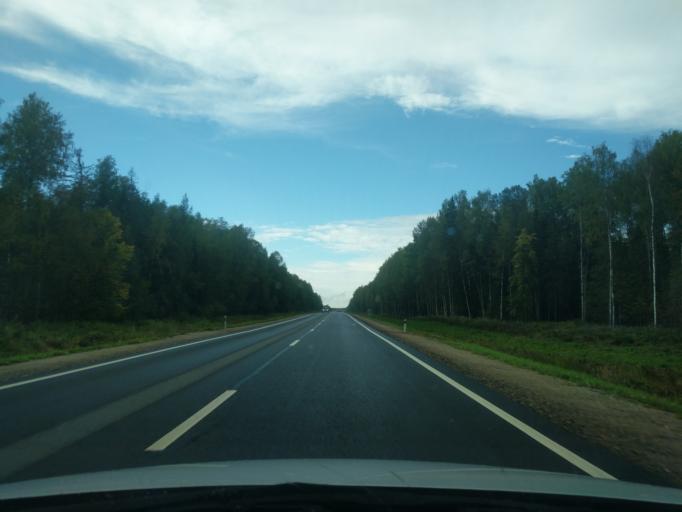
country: RU
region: Kostroma
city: Ostrovskoye
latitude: 57.8142
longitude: 42.0186
